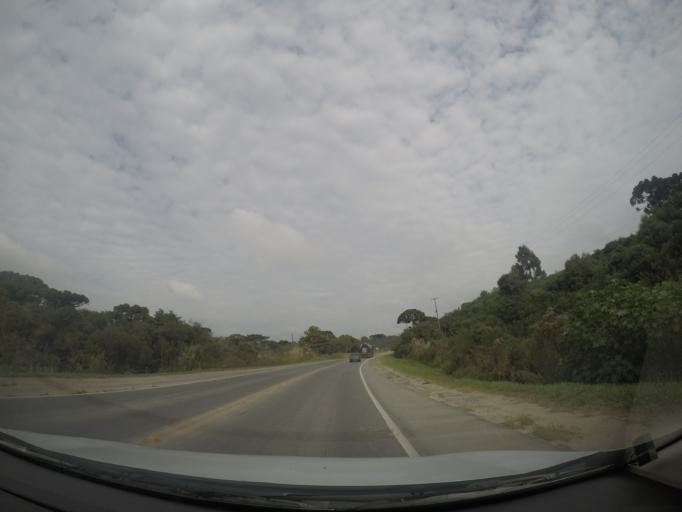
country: BR
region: Parana
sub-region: Almirante Tamandare
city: Almirante Tamandare
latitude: -25.3382
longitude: -49.2572
